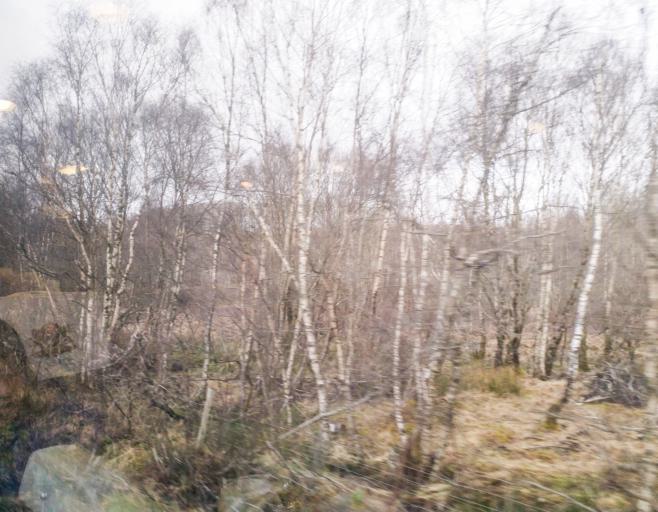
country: GB
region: Scotland
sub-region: Highland
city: Spean Bridge
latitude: 56.8877
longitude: -4.8314
